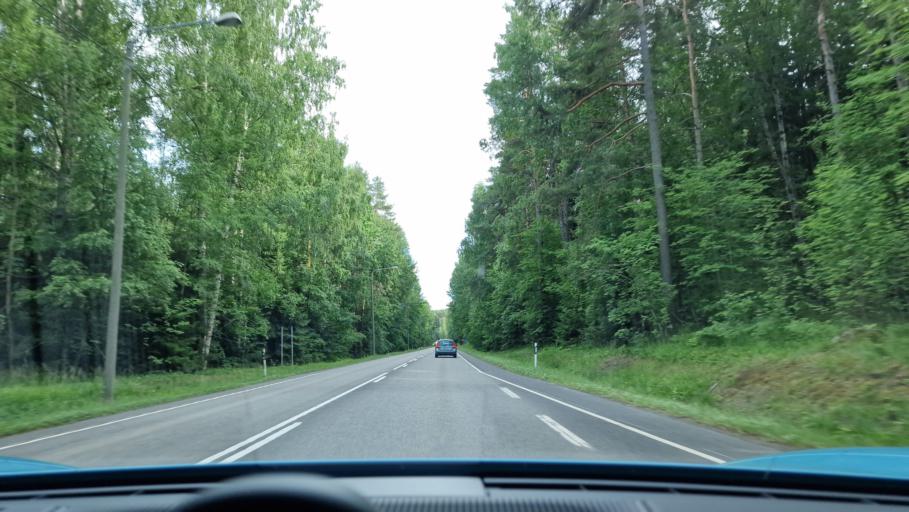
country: FI
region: Pirkanmaa
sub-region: Tampere
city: Kangasala
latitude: 61.4253
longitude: 24.1360
